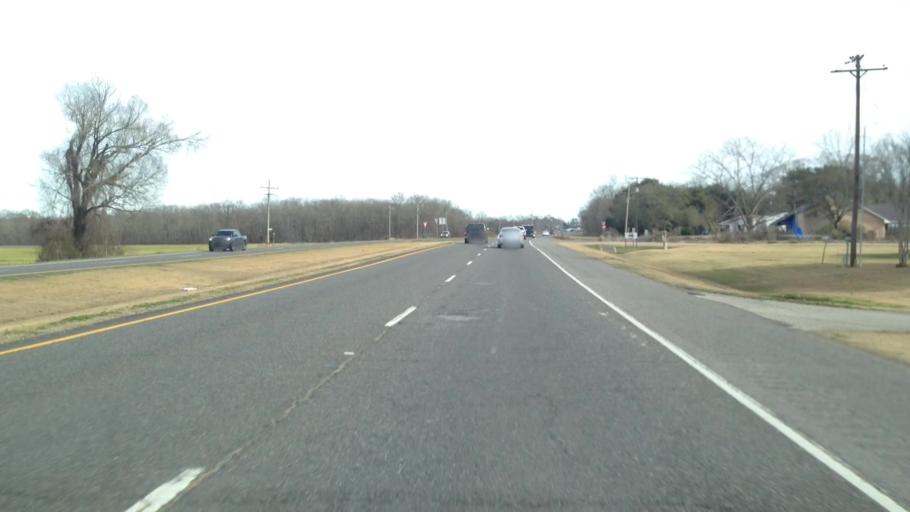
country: US
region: Louisiana
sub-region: Saint Landry Parish
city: Port Barre
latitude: 30.5478
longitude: -91.9870
